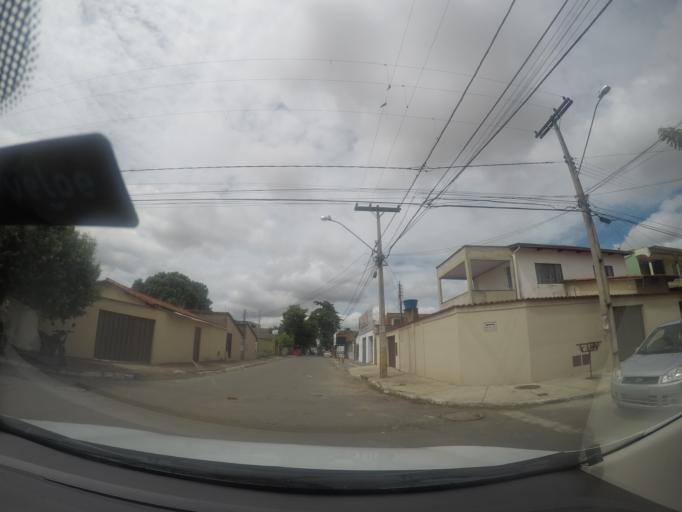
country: BR
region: Goias
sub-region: Goiania
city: Goiania
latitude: -16.6614
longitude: -49.3036
